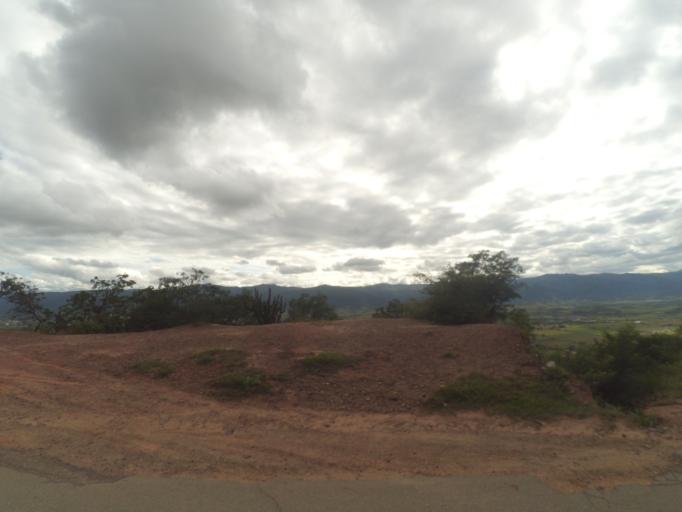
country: BO
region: Santa Cruz
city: Samaipata
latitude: -18.1647
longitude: -63.8915
